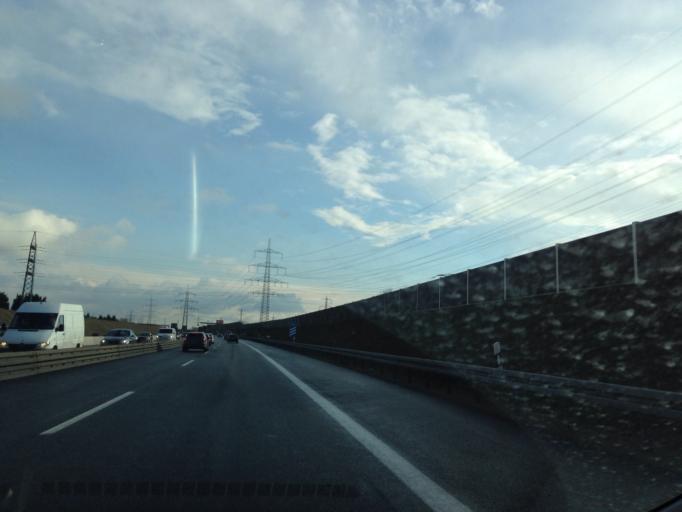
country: DE
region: North Rhine-Westphalia
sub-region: Regierungsbezirk Dusseldorf
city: Kaarst
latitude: 51.2253
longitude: 6.6387
